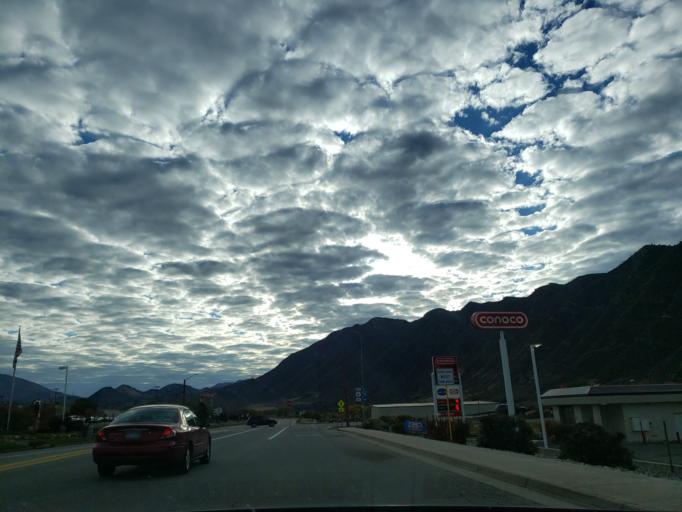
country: US
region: Colorado
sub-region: Garfield County
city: New Castle
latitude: 39.5682
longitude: -107.5171
